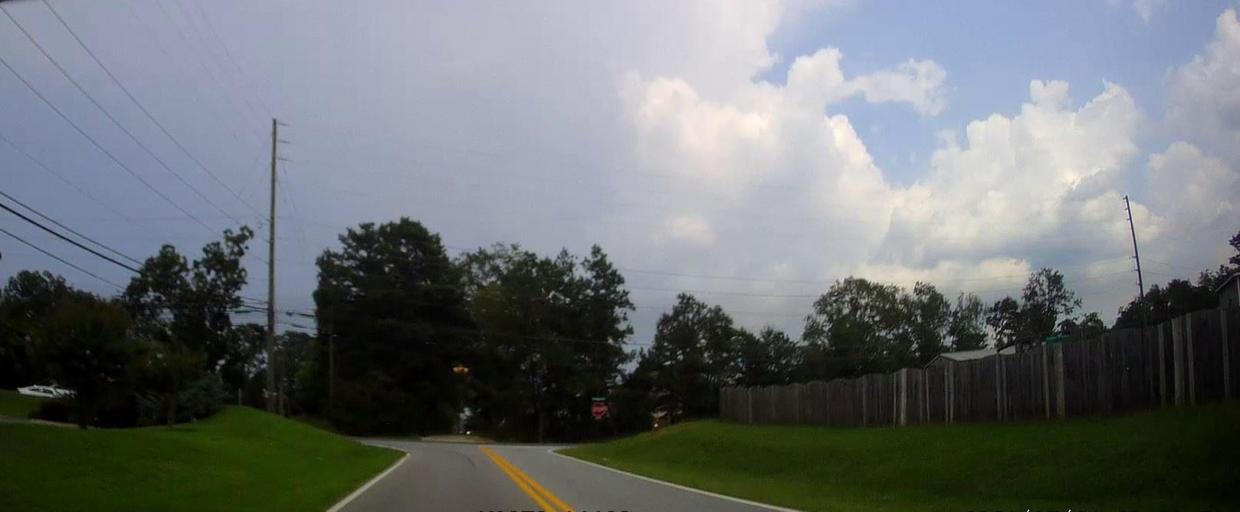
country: US
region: Georgia
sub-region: Houston County
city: Robins Air Force Base
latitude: 32.5683
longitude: -83.5887
